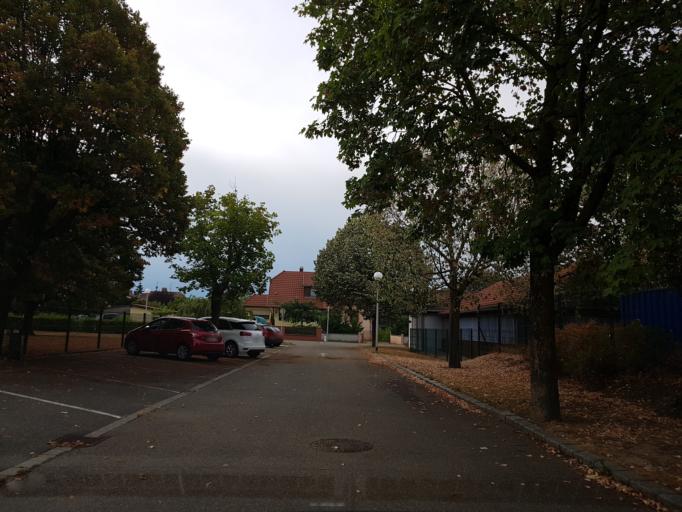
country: FR
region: Alsace
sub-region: Departement du Haut-Rhin
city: Kingersheim
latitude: 47.8006
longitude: 7.3151
